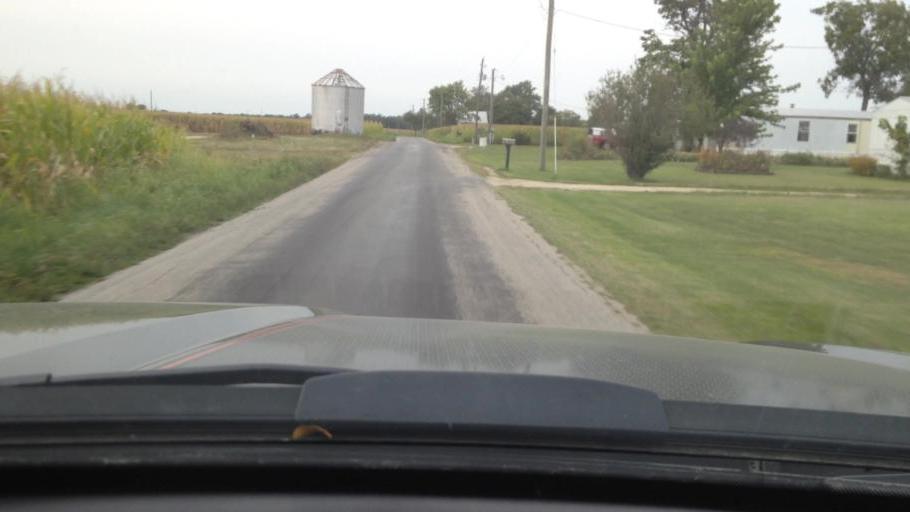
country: US
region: Indiana
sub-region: Randolph County
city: Winchester
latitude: 40.2200
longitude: -84.9567
